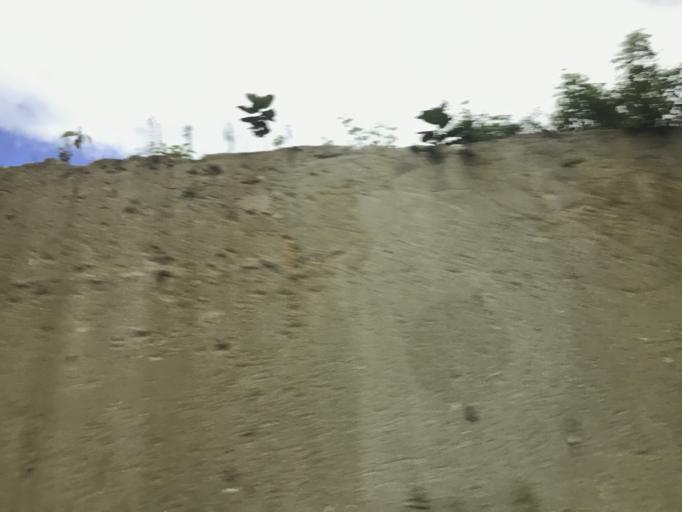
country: GT
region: Chimaltenango
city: Parramos
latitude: 14.6255
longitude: -90.8050
